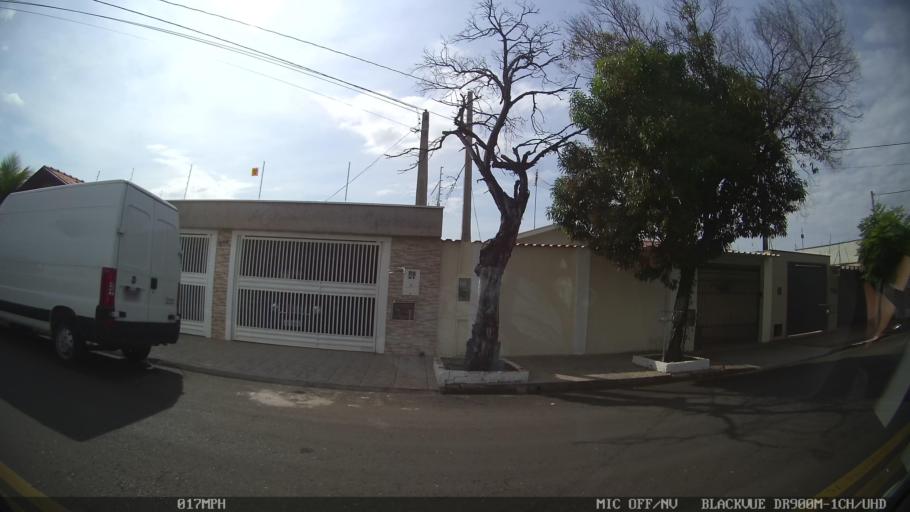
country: BR
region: Sao Paulo
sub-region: Piracicaba
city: Piracicaba
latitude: -22.7147
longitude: -47.6674
